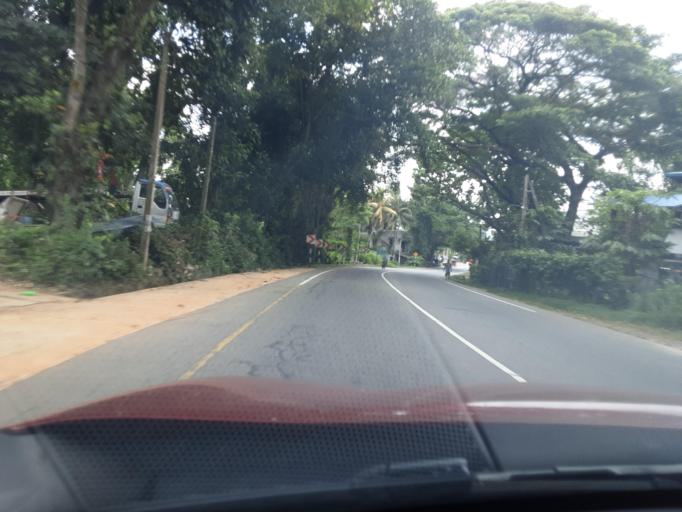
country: LK
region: North Western
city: Kurunegala
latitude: 7.4376
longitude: 80.2079
